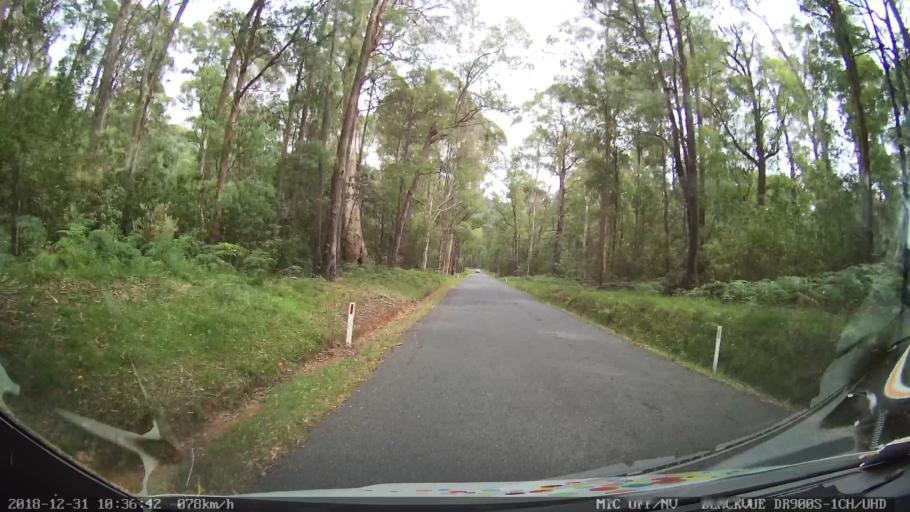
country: AU
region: New South Wales
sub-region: Snowy River
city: Jindabyne
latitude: -36.4235
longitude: 148.1711
